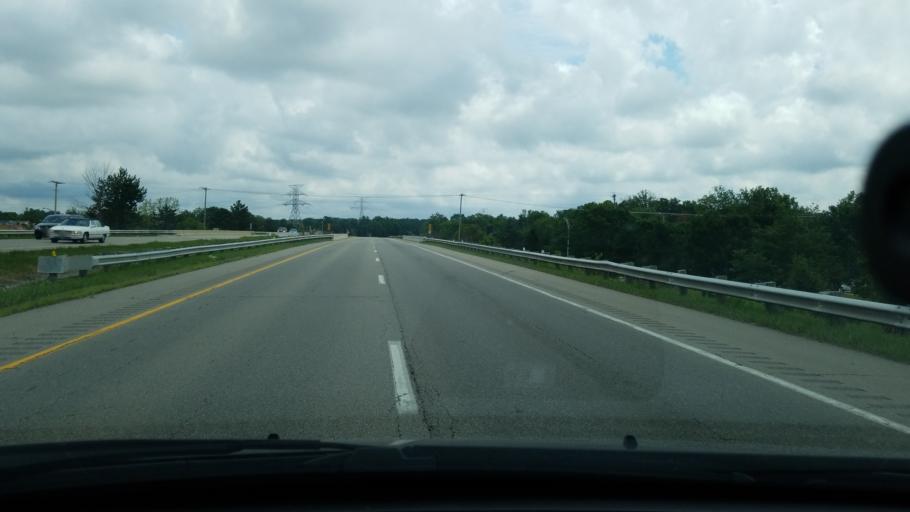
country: US
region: Ohio
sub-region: Lorain County
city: Amherst
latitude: 41.4138
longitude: -82.2106
